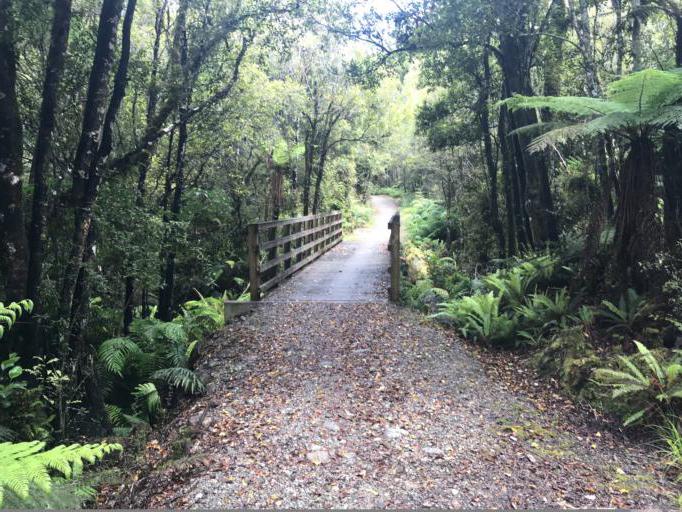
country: NZ
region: West Coast
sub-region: Westland District
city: Hokitika
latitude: -42.7615
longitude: 171.2447
